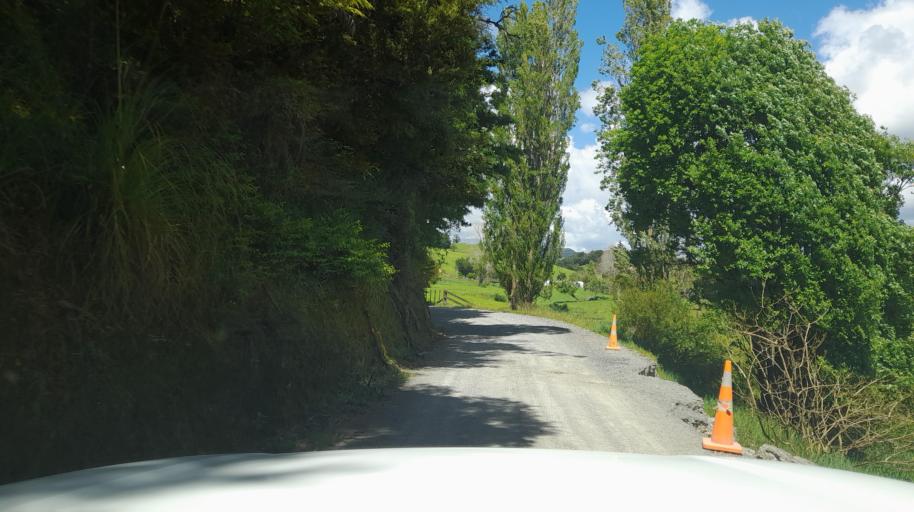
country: NZ
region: Northland
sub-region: Far North District
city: Kaitaia
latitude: -35.1195
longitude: 173.3968
